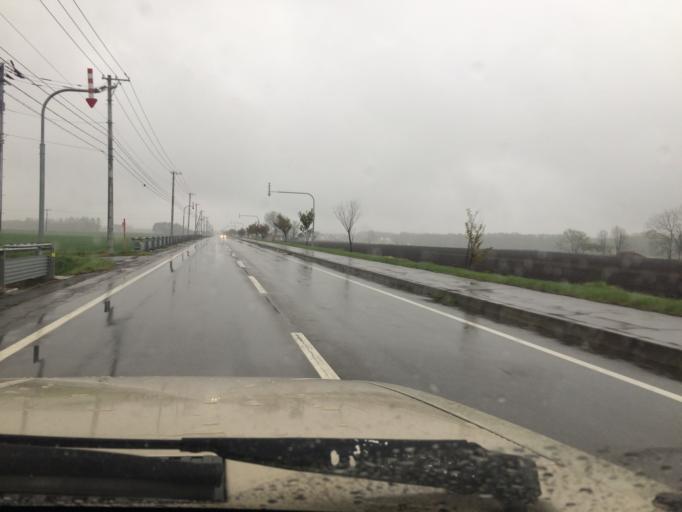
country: JP
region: Hokkaido
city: Obihiro
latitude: 42.8825
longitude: 143.0331
